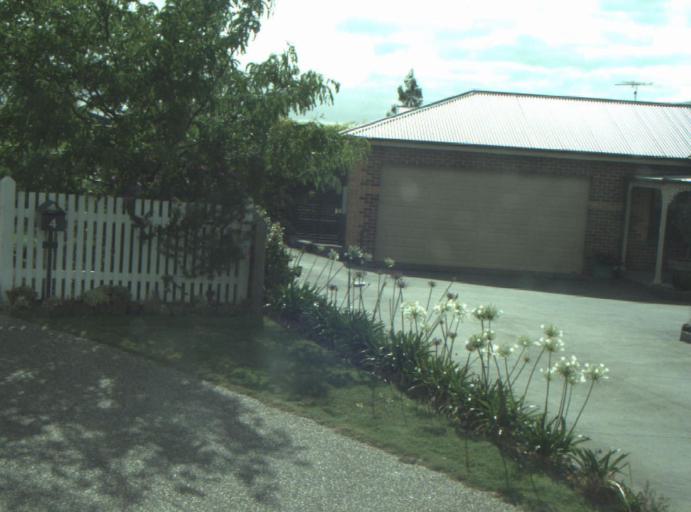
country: AU
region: Victoria
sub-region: Greater Geelong
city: Wandana Heights
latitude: -38.2138
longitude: 144.2946
